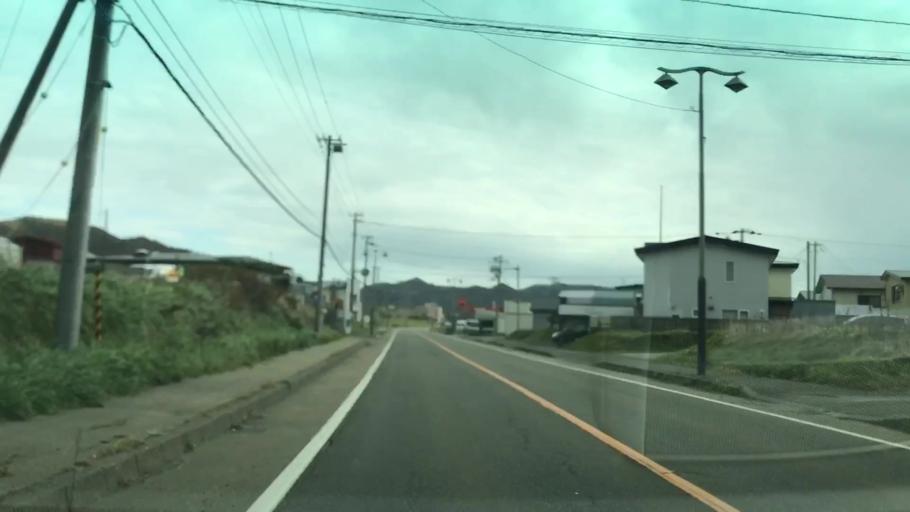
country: JP
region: Hokkaido
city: Shizunai-furukawacho
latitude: 42.0118
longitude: 143.1497
